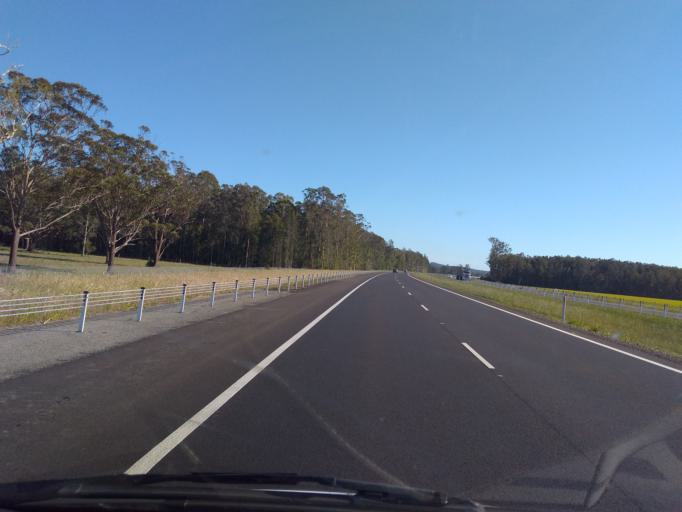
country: AU
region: New South Wales
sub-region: Port Macquarie-Hastings
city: North Shore
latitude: -31.3465
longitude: 152.8082
